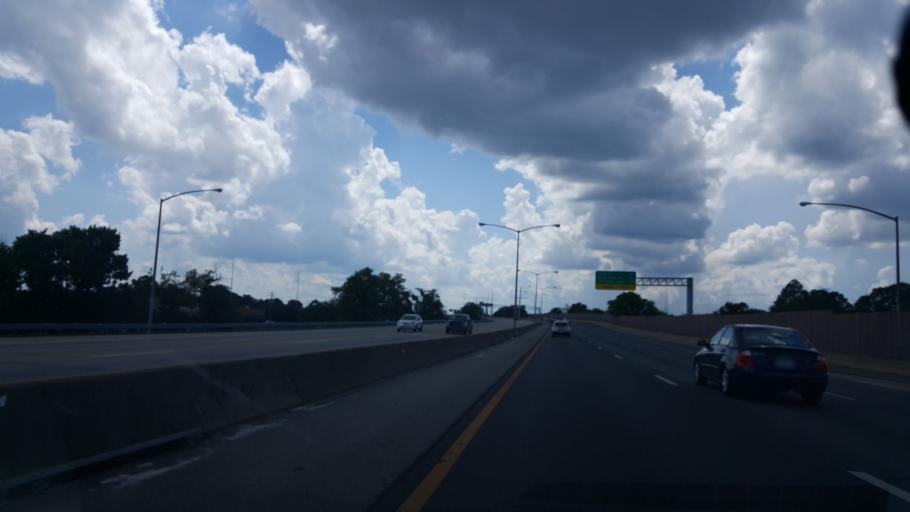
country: US
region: Virginia
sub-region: City of Newport News
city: Newport News
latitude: 36.9952
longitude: -76.4169
